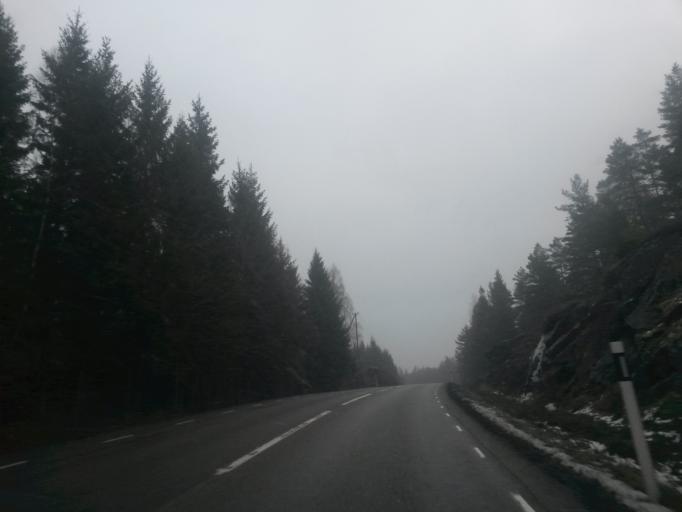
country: SE
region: Vaestra Goetaland
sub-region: Alingsas Kommun
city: Sollebrunn
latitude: 58.1885
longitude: 12.4267
